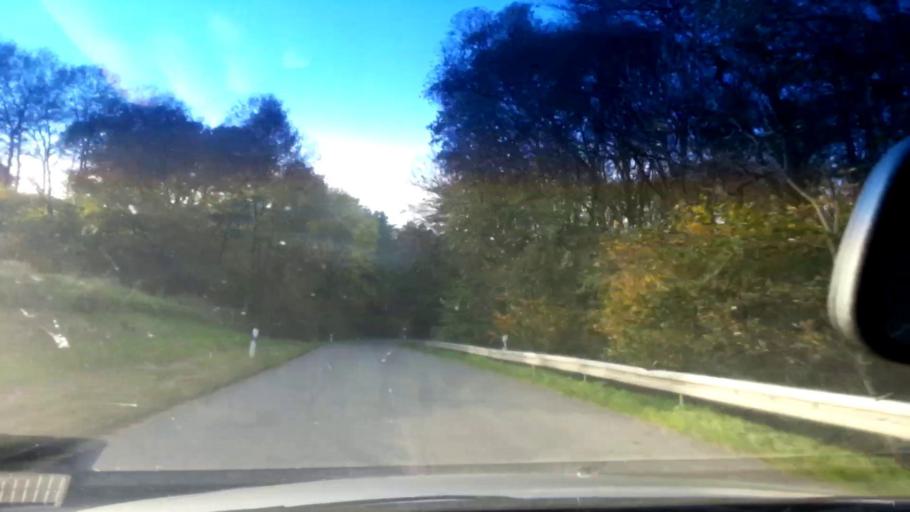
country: DE
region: Bavaria
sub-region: Upper Franconia
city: Ebensfeld
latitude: 50.0355
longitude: 10.9646
